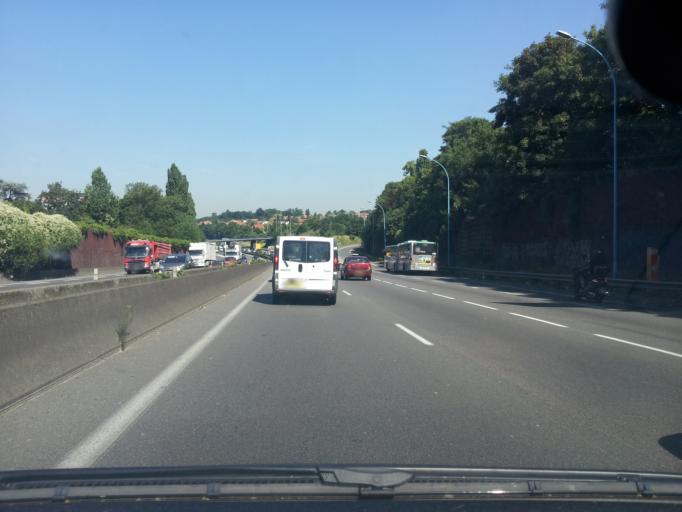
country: FR
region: Ile-de-France
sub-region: Departement de l'Essonne
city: Savigny-sur-Orge
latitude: 48.6748
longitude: 2.3417
